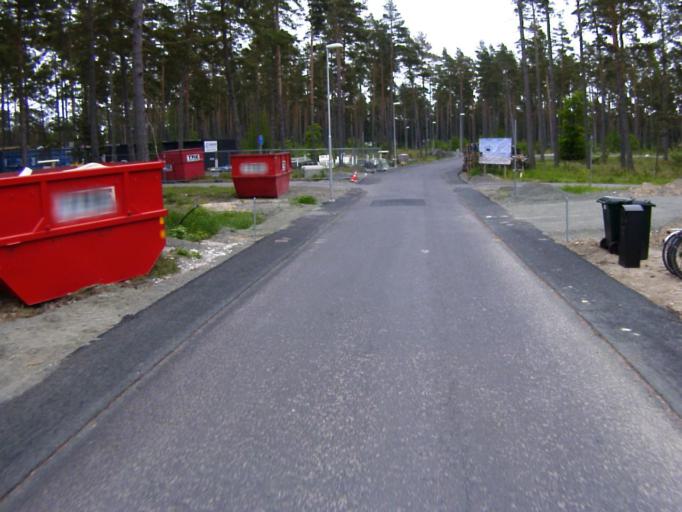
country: SE
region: Skane
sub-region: Kristianstads Kommun
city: Ahus
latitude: 55.9078
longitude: 14.2704
